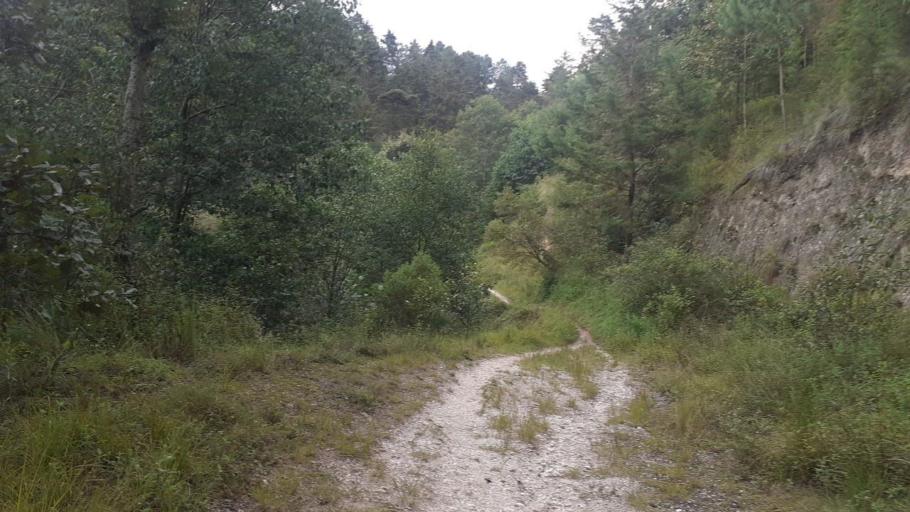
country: GT
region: Quetzaltenango
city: Cantel
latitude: 14.8210
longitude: -91.4467
